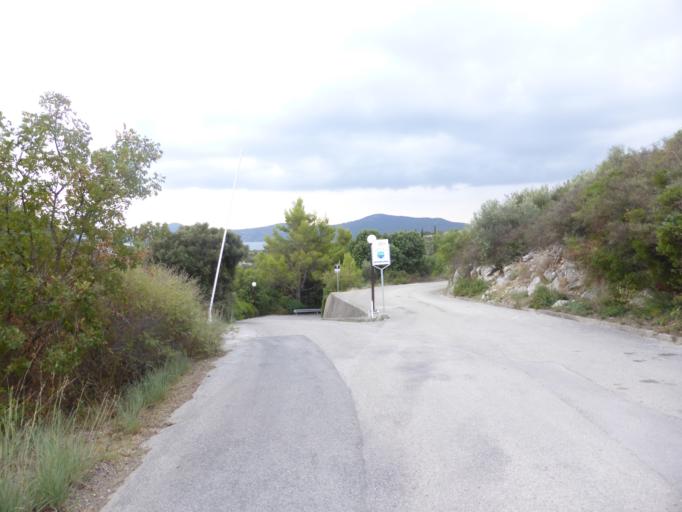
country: HR
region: Dubrovacko-Neretvanska
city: Podgora
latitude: 42.7809
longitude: 17.8686
